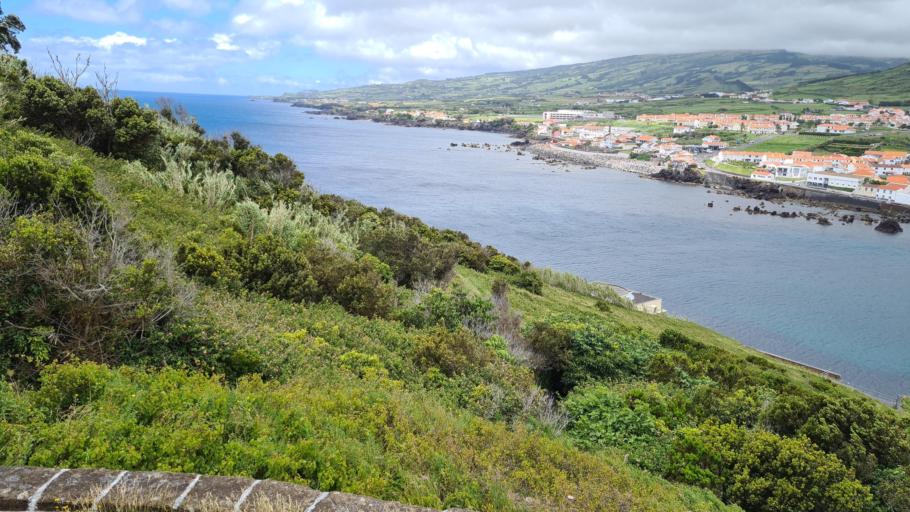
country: PT
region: Azores
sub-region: Horta
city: Horta
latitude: 38.5221
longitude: -28.6270
